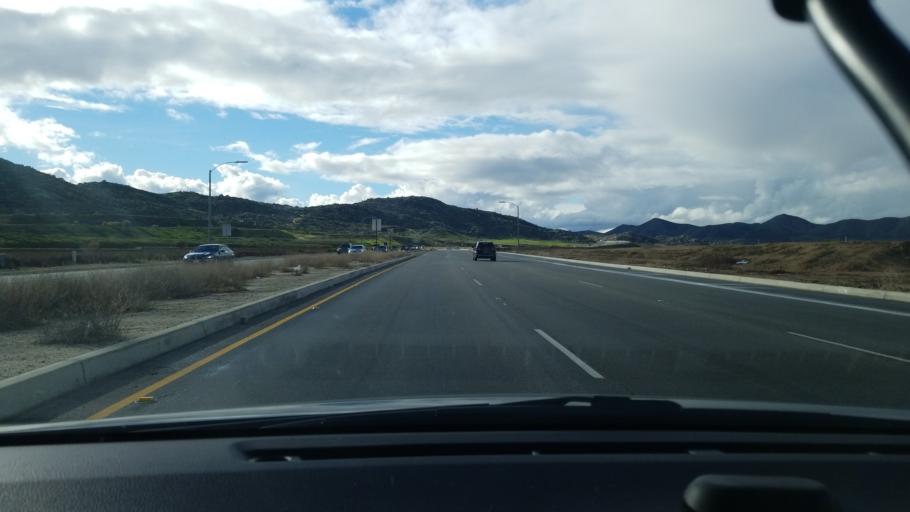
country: US
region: California
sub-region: Riverside County
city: Winchester
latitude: 33.6926
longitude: -117.1215
